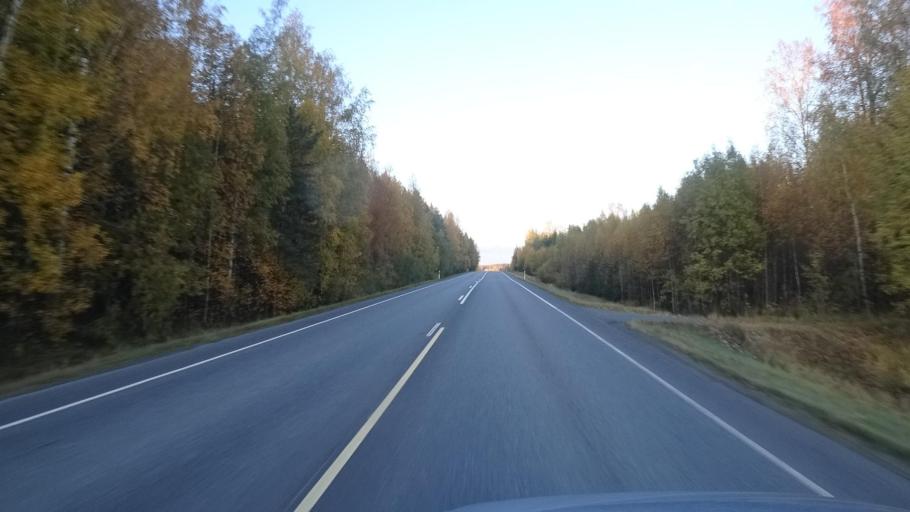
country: FI
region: Haeme
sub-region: Forssa
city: Jokioinen
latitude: 60.7969
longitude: 23.5095
